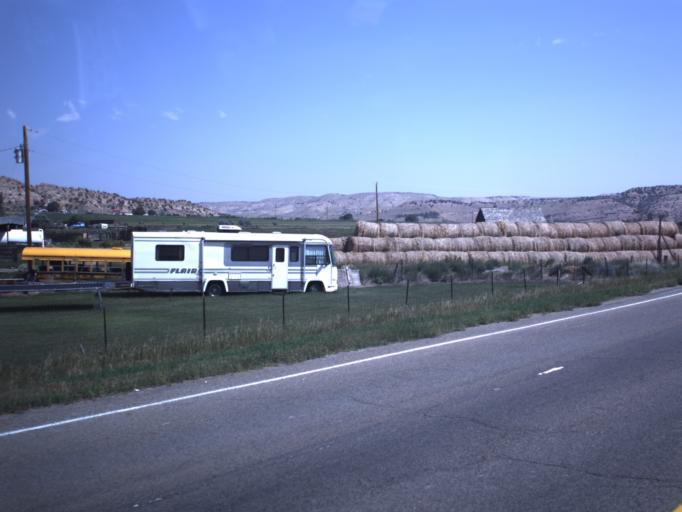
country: US
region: Utah
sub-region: Daggett County
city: Manila
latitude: 40.9929
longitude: -109.6849
